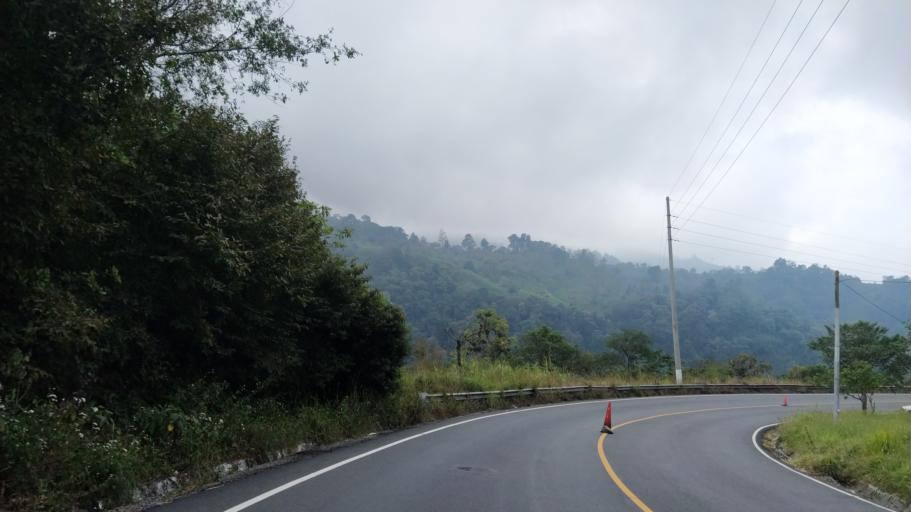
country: GT
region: Quetzaltenango
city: Zunil
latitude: 14.7331
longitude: -91.5205
